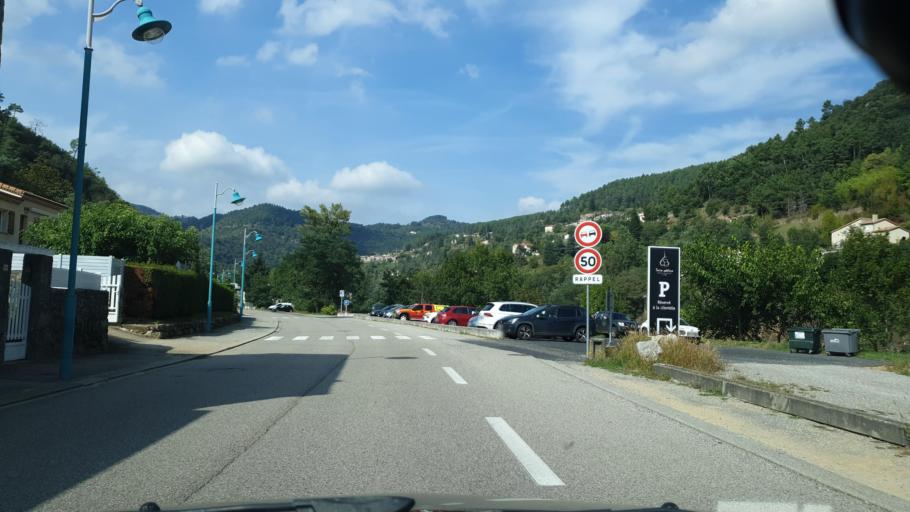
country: FR
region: Rhone-Alpes
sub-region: Departement de l'Ardeche
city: Saint-Sauveur-de-Montagut
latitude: 44.8181
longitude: 4.5952
